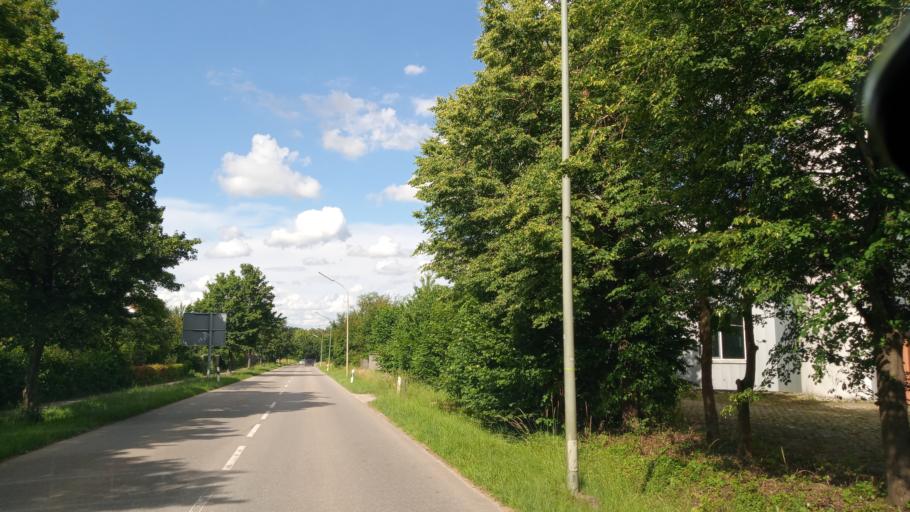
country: DE
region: Bavaria
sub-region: Upper Bavaria
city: Vierkirchen
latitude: 48.3579
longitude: 11.4397
